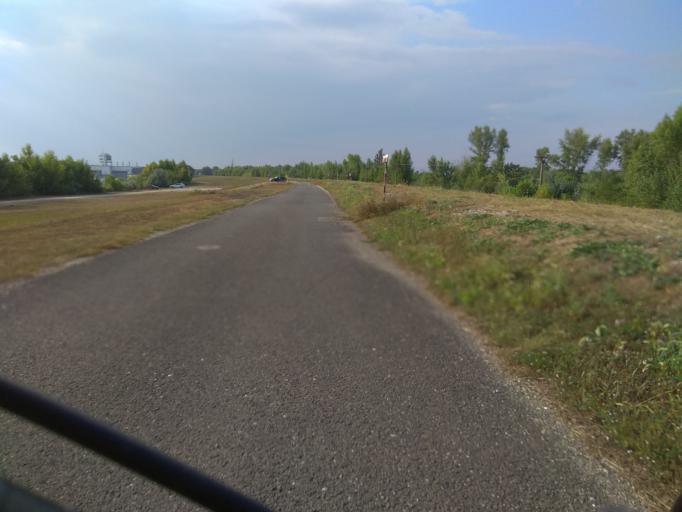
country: SK
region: Trnavsky
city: Gabcikovo
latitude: 47.8738
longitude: 17.5538
